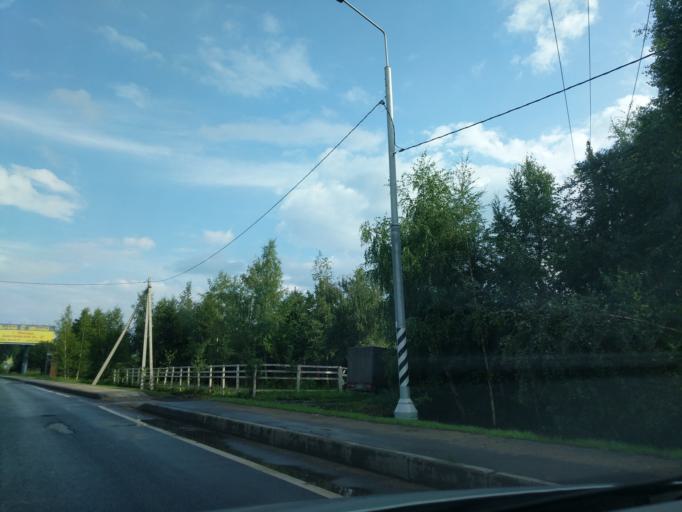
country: RU
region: Moskovskaya
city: Lobnya
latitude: 56.0093
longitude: 37.5082
